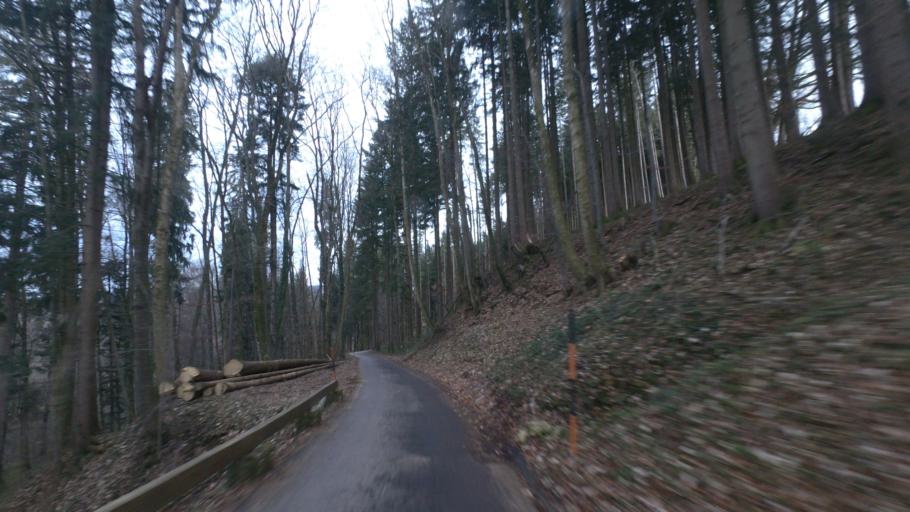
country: DE
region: Bavaria
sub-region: Upper Bavaria
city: Ubersee
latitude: 47.8072
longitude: 12.5192
